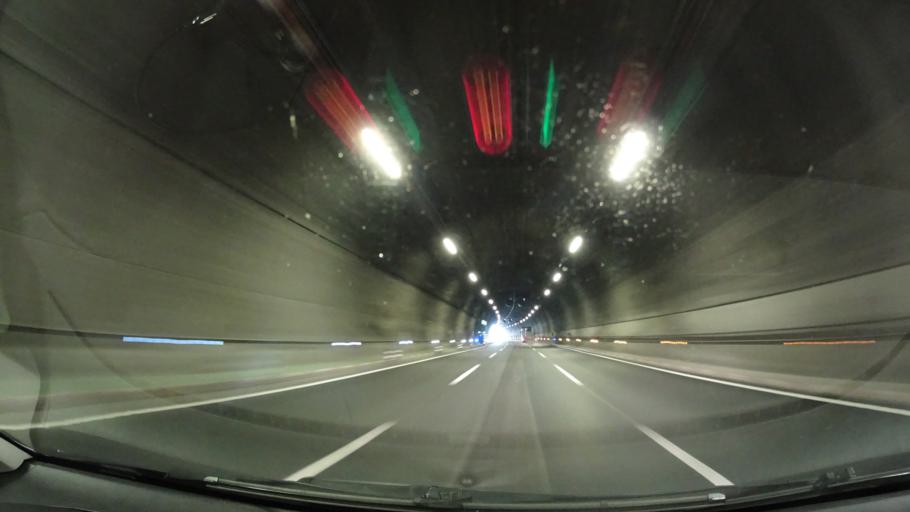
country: ES
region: Madrid
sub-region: Provincia de Madrid
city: Somosierra
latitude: 41.1347
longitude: -3.5829
